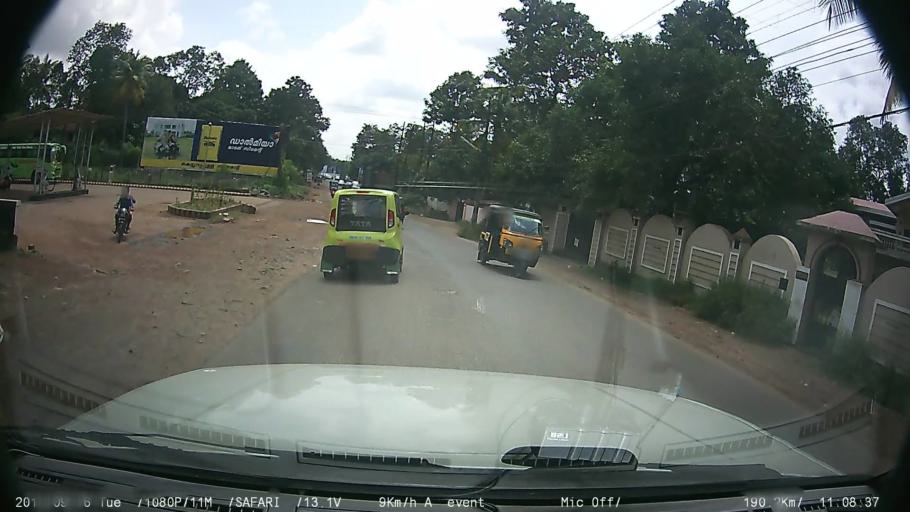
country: IN
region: Kerala
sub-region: Kottayam
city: Kottayam
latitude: 9.5265
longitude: 76.5210
